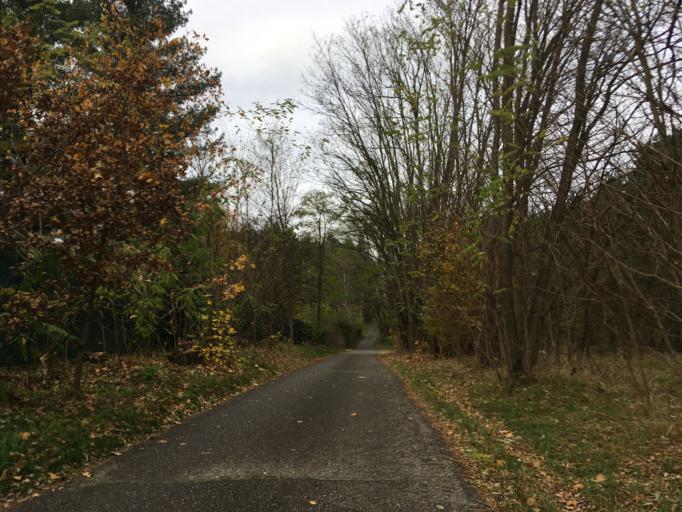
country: DE
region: Brandenburg
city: Mixdorf
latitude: 52.1014
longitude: 14.4327
